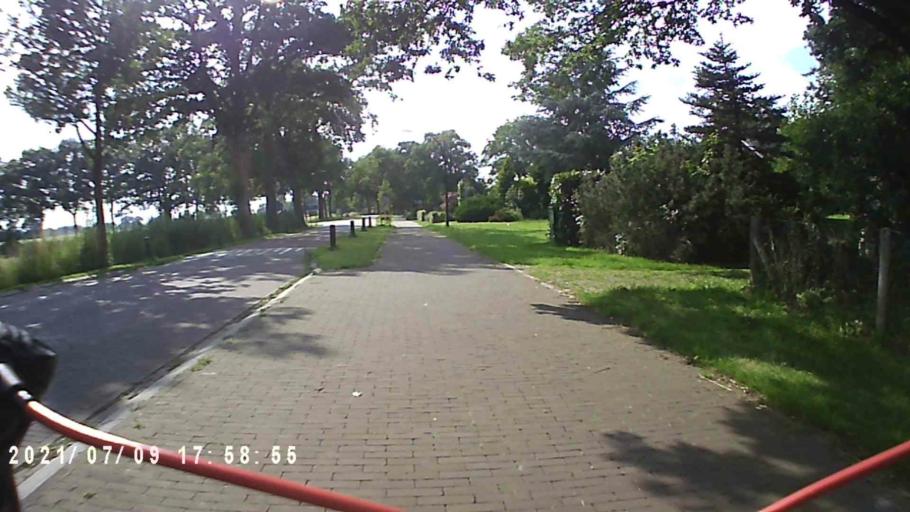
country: NL
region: Groningen
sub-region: Gemeente Vlagtwedde
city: Vlagtwedde
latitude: 53.0684
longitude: 7.0696
